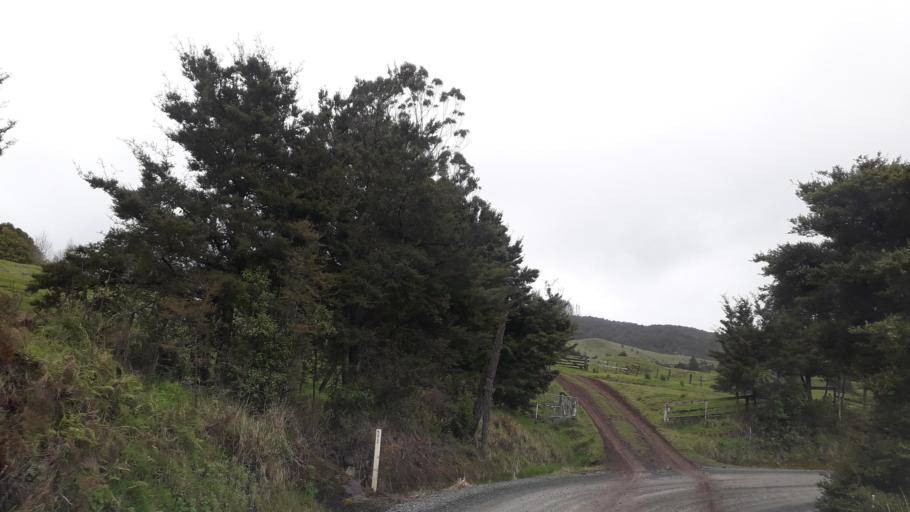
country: NZ
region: Northland
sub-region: Far North District
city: Kerikeri
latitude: -35.1301
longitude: 173.7399
